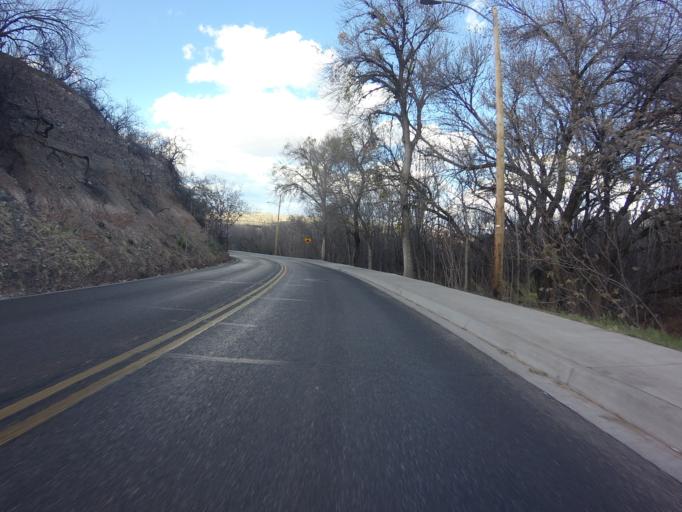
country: US
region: Arizona
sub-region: Yavapai County
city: Cottonwood
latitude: 34.7439
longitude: -112.0264
